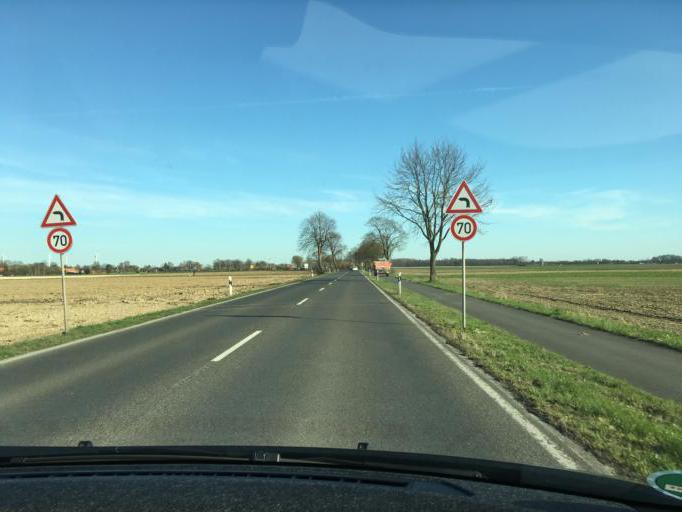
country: DE
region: North Rhine-Westphalia
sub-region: Regierungsbezirk Dusseldorf
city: Korschenbroich
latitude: 51.1880
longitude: 6.5459
